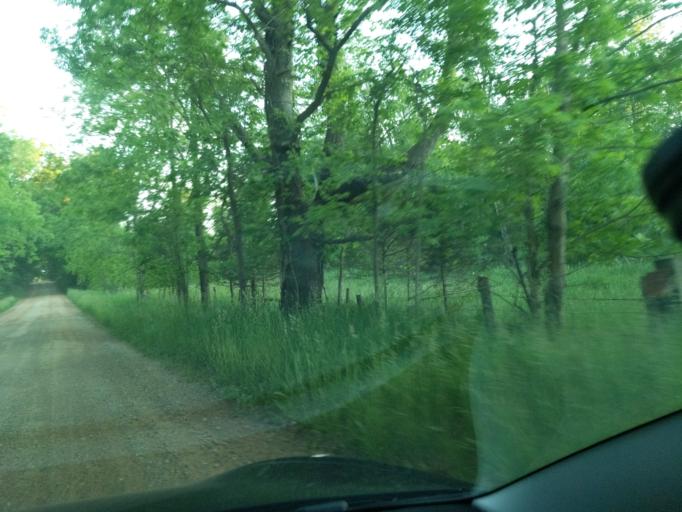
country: US
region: Michigan
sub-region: Barry County
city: Nashville
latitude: 42.5357
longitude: -85.1133
